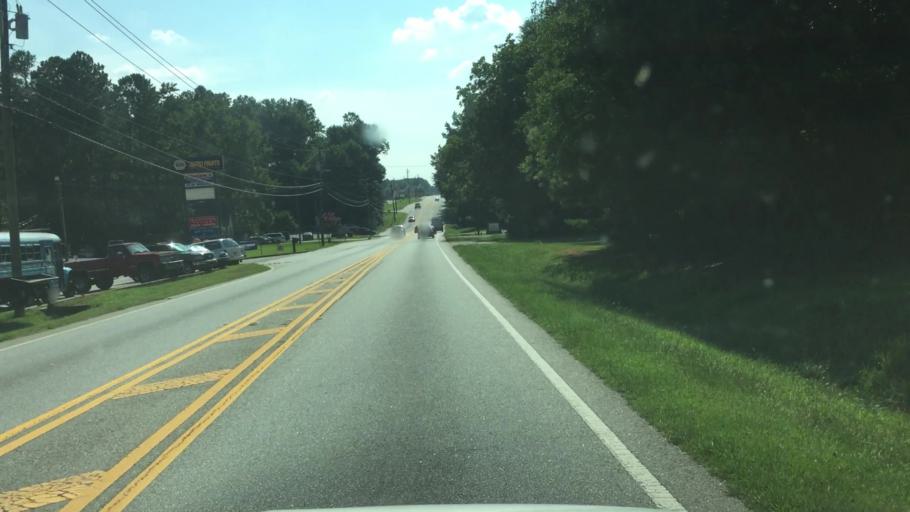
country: US
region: Georgia
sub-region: Barrow County
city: Auburn
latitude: 34.0122
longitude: -83.8332
